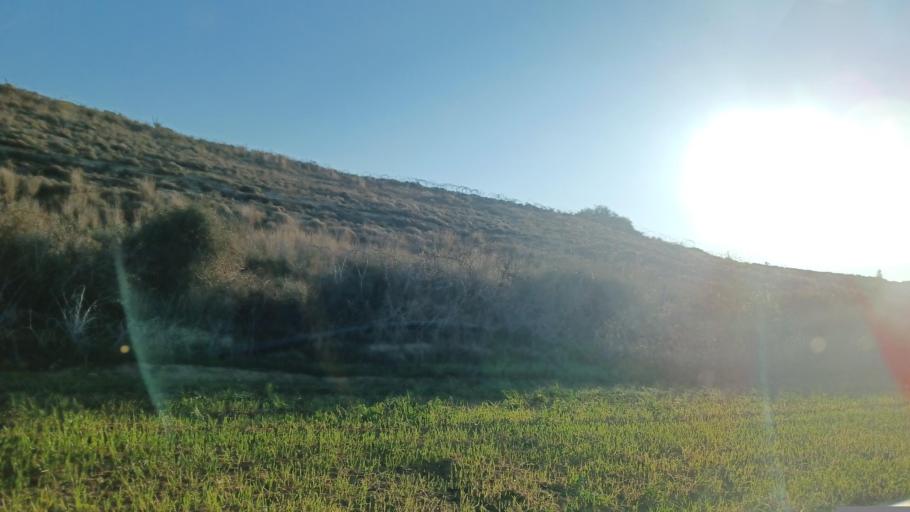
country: CY
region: Lefkosia
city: Mammari
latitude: 35.1526
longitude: 33.2640
